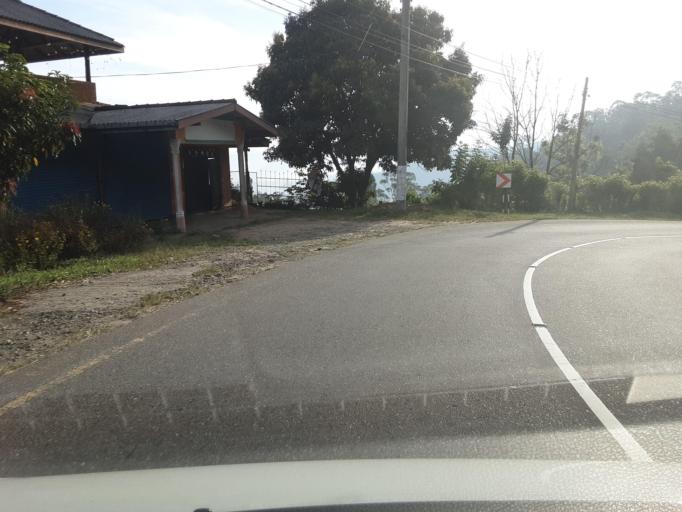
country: LK
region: Uva
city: Badulla
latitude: 6.9393
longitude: 81.0005
